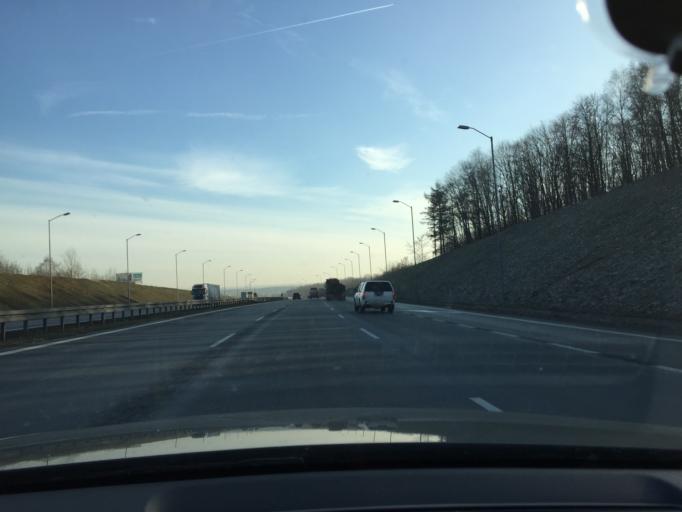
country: PL
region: Silesian Voivodeship
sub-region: Ruda Slaska
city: Ruda Slaska
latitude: 50.2507
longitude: 18.8851
